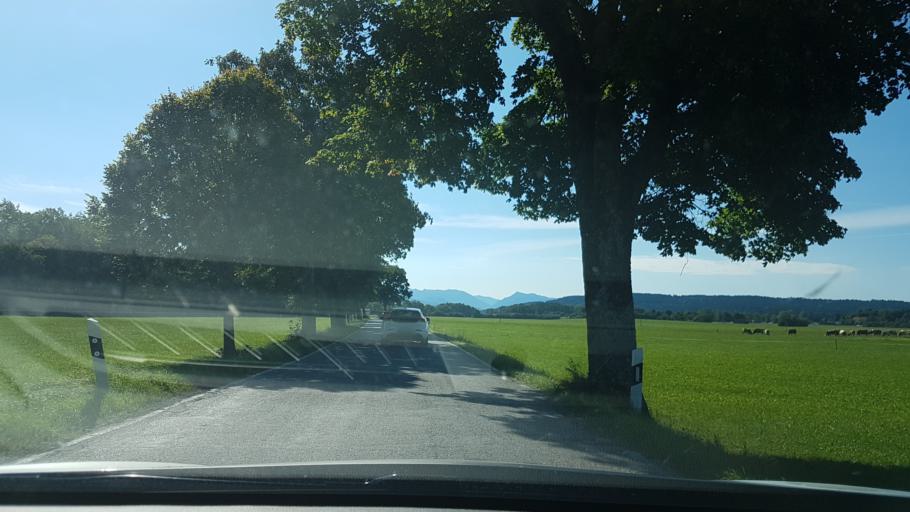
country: DE
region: Bavaria
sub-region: Upper Bavaria
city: Valley
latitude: 47.8803
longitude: 11.7793
